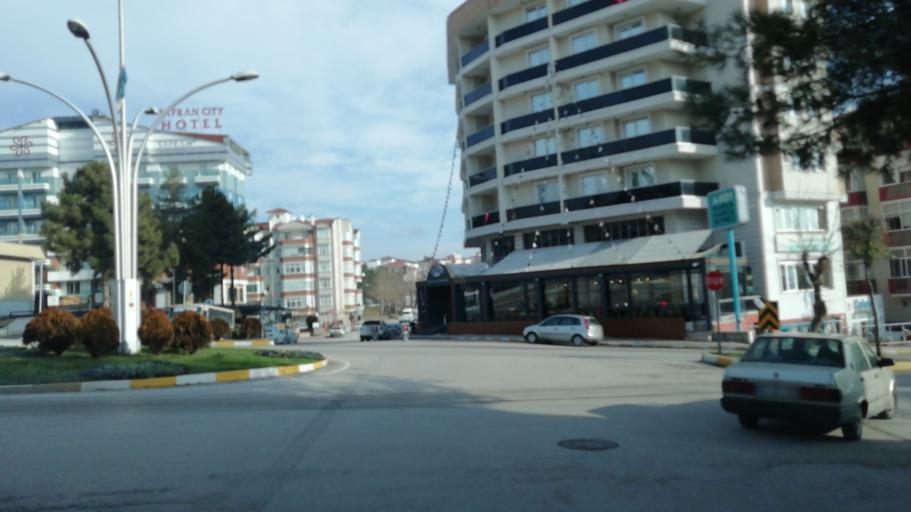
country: TR
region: Karabuk
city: Safranbolu
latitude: 41.2546
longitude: 32.6766
